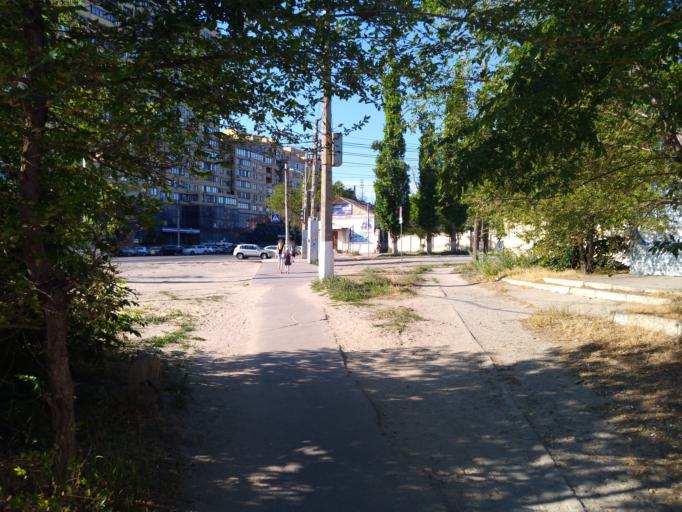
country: RU
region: Volgograd
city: Volgograd
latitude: 48.7107
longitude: 44.5038
